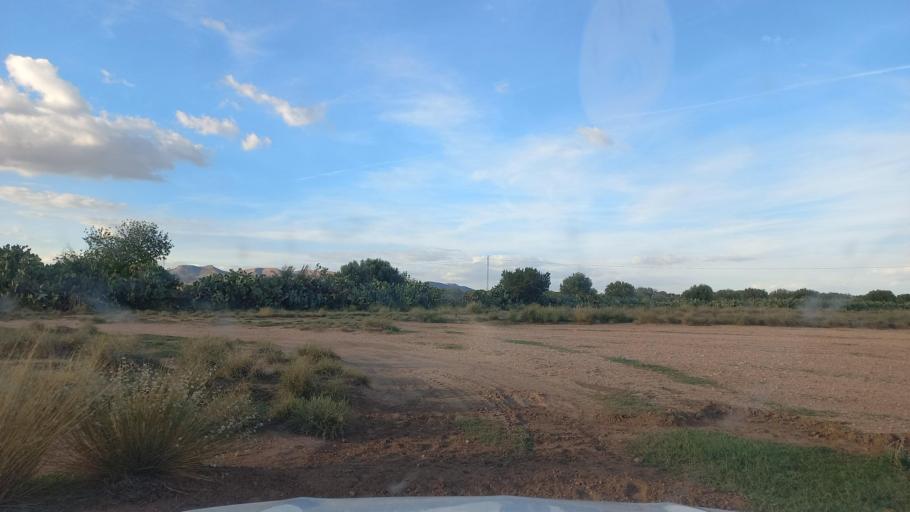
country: TN
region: Al Qasrayn
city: Sbiba
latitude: 35.3533
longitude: 9.0371
